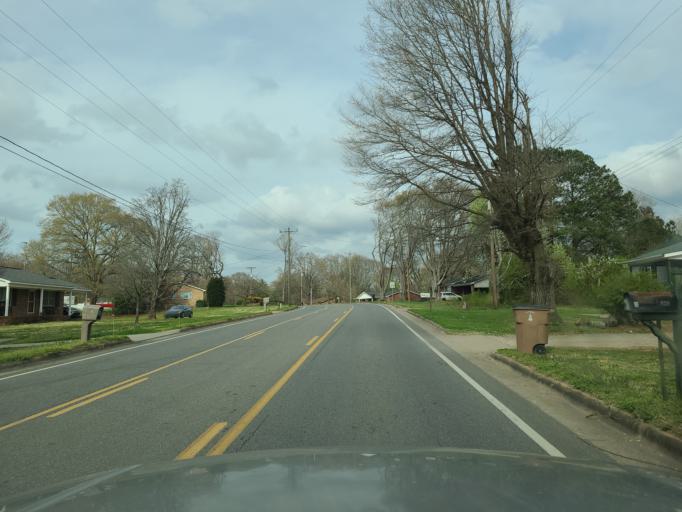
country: US
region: North Carolina
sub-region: Cleveland County
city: Shelby
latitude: 35.2762
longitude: -81.5642
